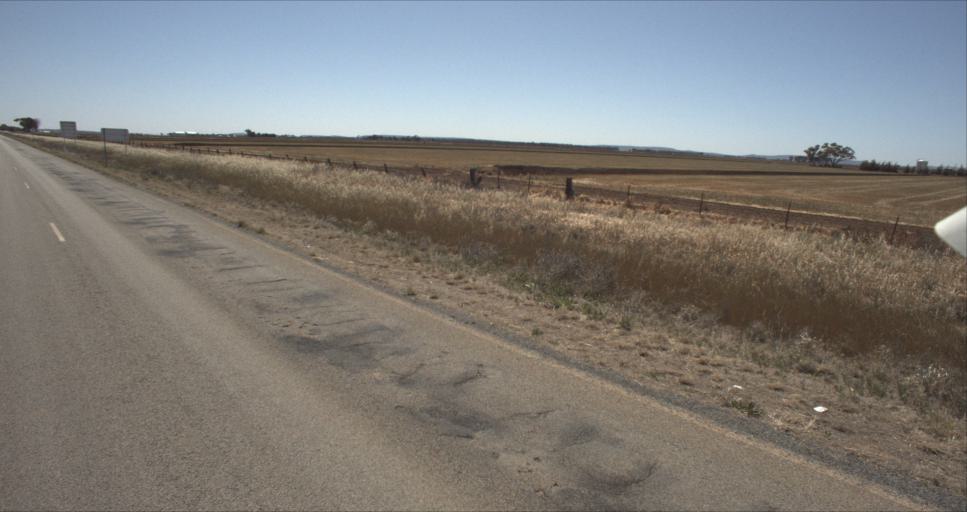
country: AU
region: New South Wales
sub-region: Leeton
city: Leeton
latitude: -34.5179
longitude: 146.2838
